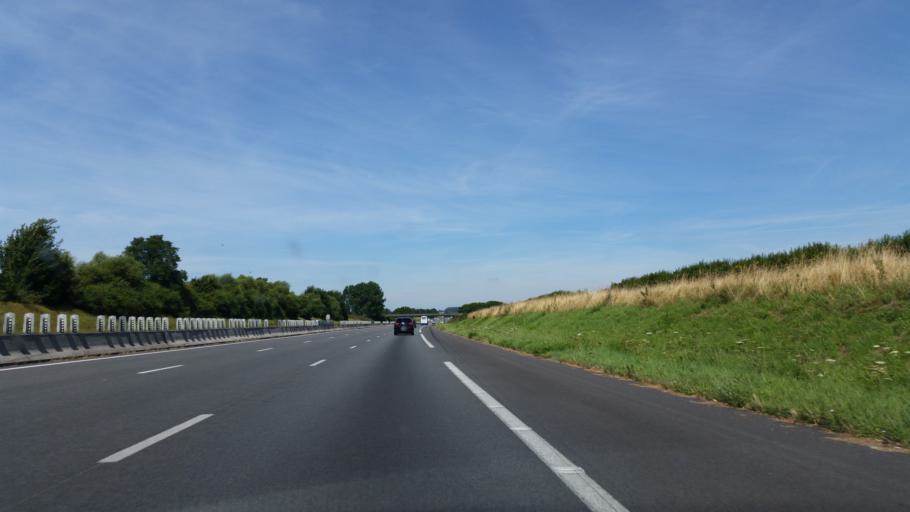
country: FR
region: Nord-Pas-de-Calais
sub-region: Departement du Pas-de-Calais
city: Bapaume
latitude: 50.0478
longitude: 2.8762
